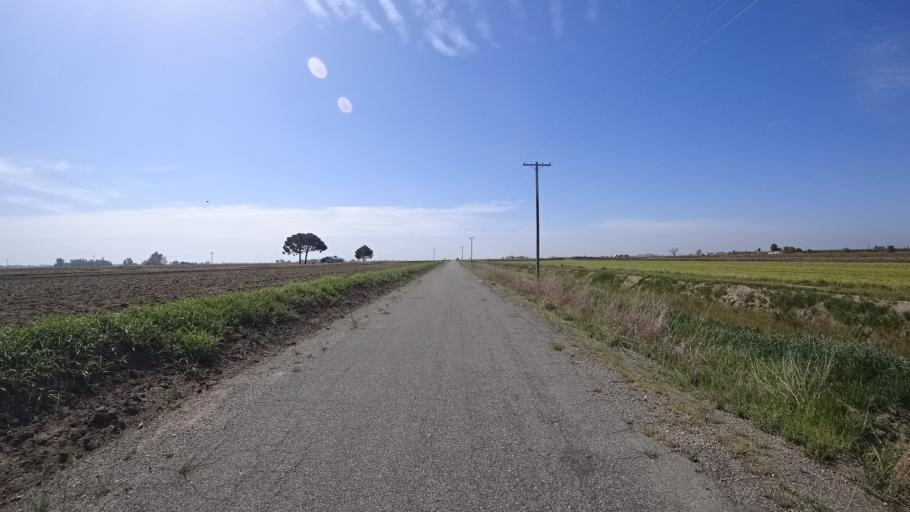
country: US
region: California
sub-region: Glenn County
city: Willows
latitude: 39.6041
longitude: -122.0744
